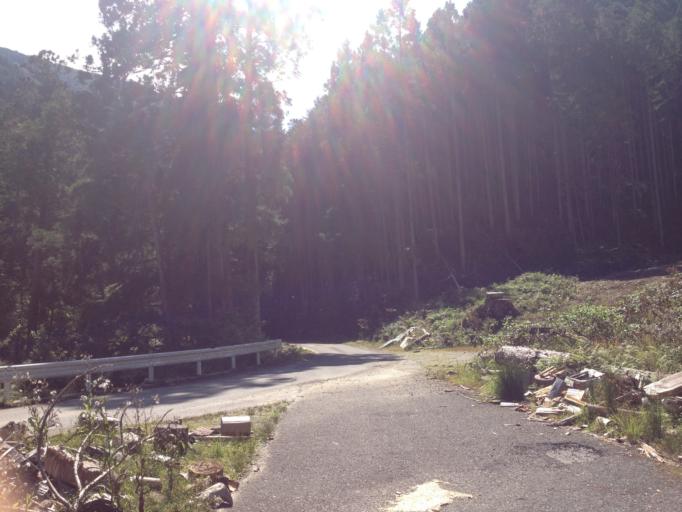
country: JP
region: Nara
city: Yoshino-cho
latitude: 34.3159
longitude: 135.9322
